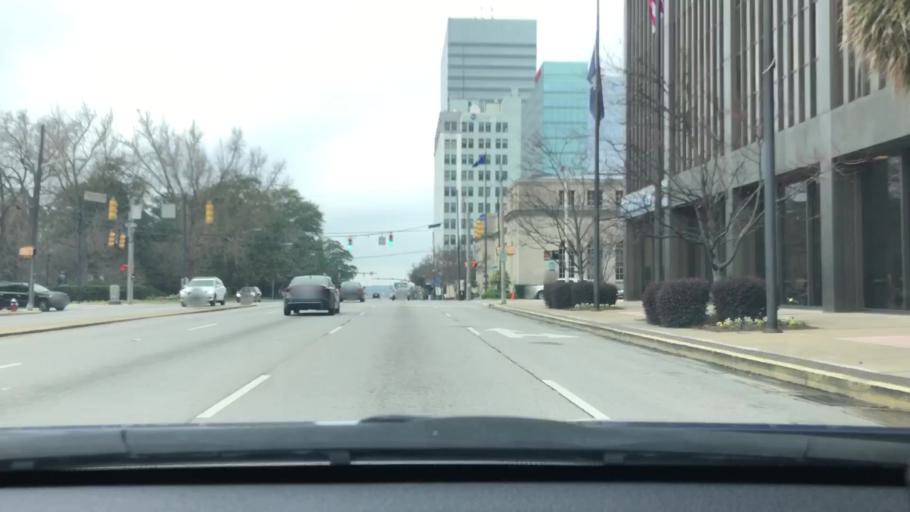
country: US
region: South Carolina
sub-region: Richland County
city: Columbia
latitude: 34.0020
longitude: -81.0314
